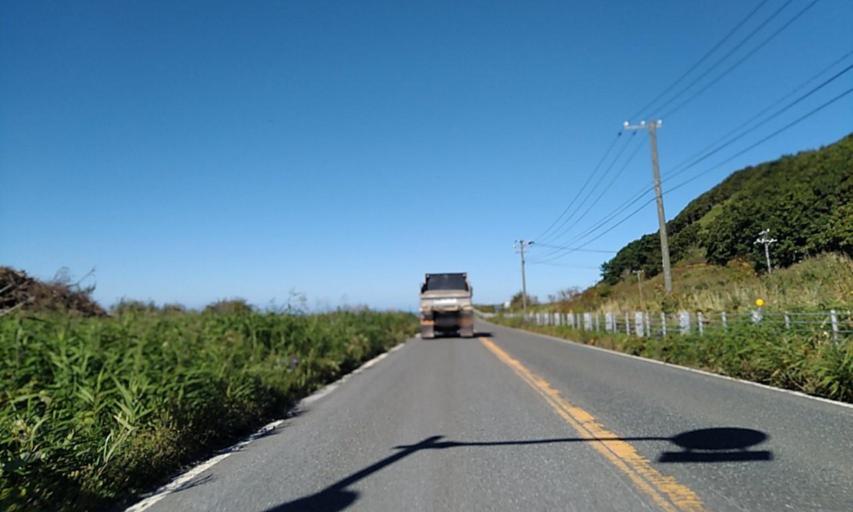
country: JP
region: Hokkaido
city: Shizunai-furukawacho
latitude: 42.4503
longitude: 142.1907
